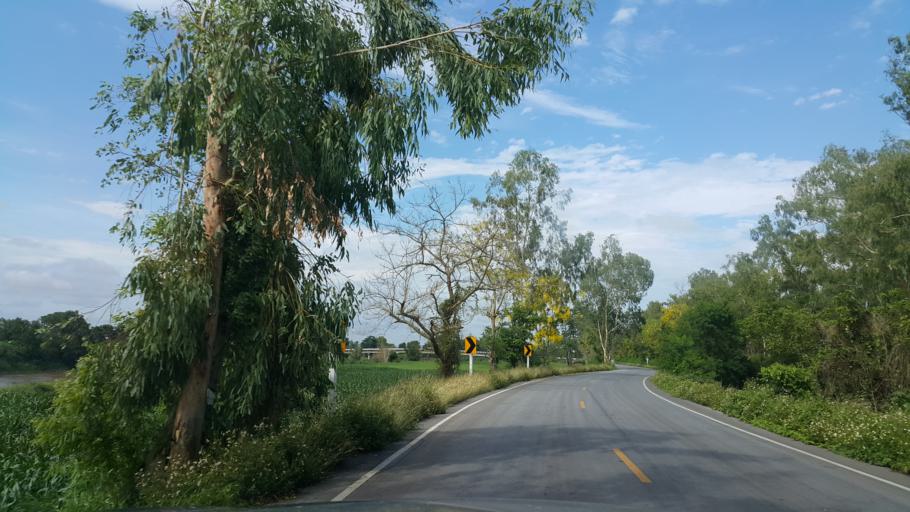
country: TH
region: Chiang Rai
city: Wiang Chai
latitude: 19.9574
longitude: 99.9418
